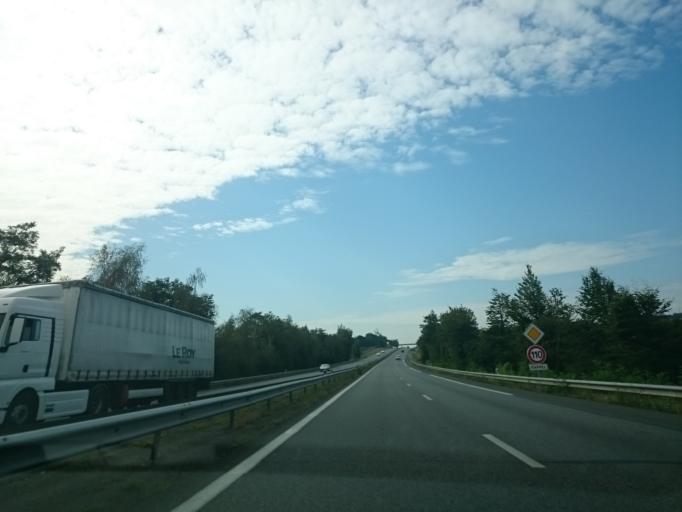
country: FR
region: Brittany
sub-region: Departement d'Ille-et-Vilaine
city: Pance
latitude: 47.8837
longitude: -1.6897
